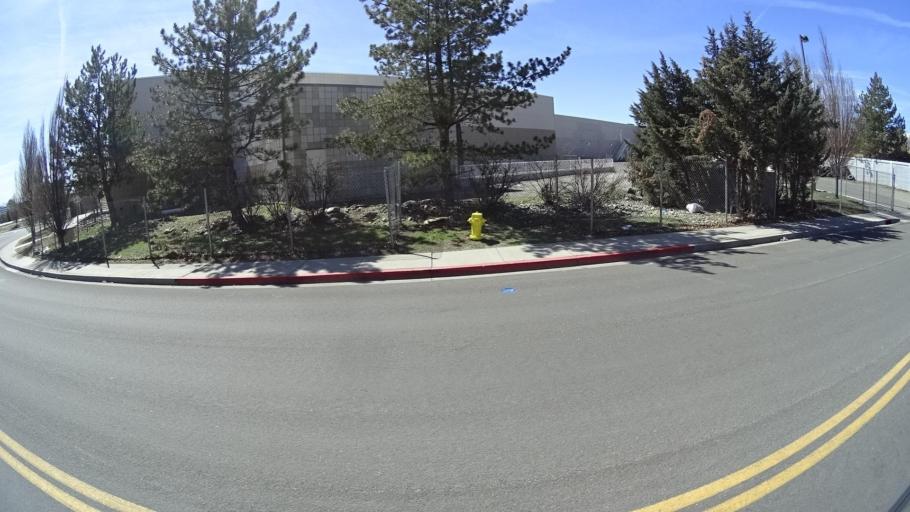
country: US
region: Nevada
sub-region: Washoe County
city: Sparks
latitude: 39.5483
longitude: -119.7788
